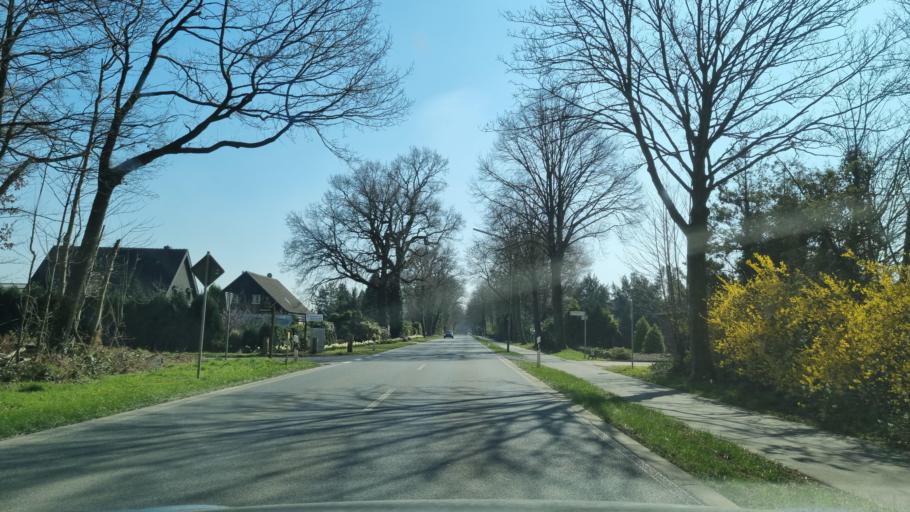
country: DE
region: North Rhine-Westphalia
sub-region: Regierungsbezirk Dusseldorf
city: Goch
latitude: 51.7223
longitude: 6.1289
